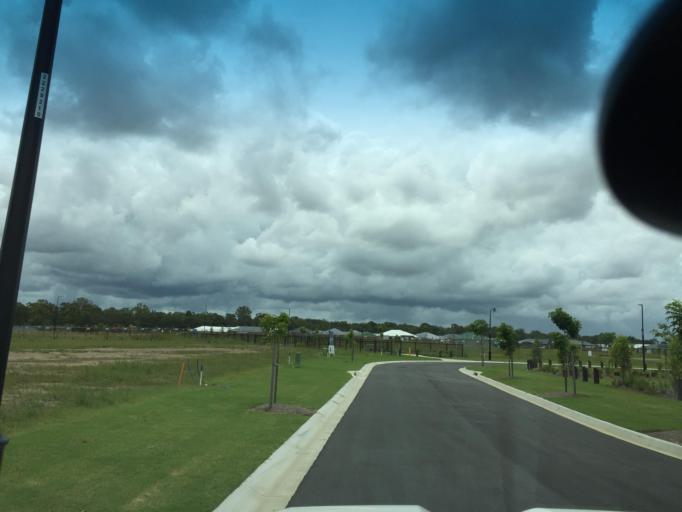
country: AU
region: Queensland
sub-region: Moreton Bay
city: Caboolture
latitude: -27.0630
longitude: 152.9221
